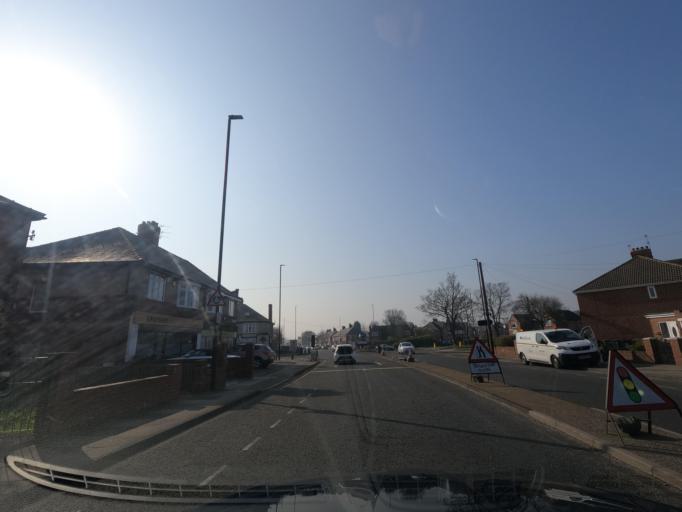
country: GB
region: England
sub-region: Newcastle upon Tyne
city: Gosforth
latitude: 54.9986
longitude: -1.5808
